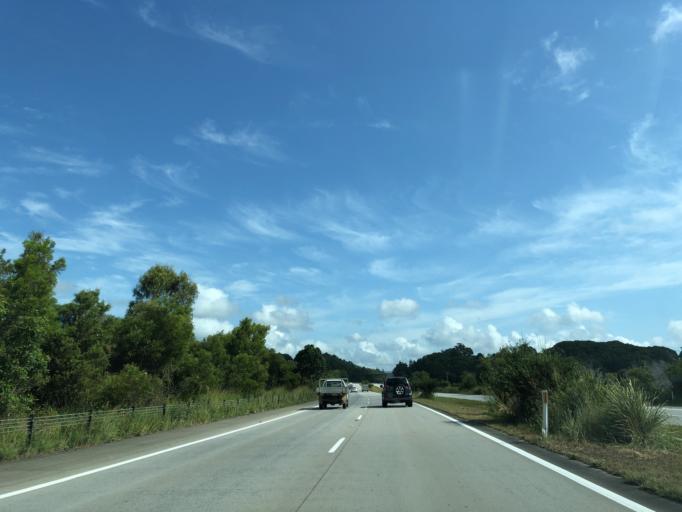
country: AU
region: New South Wales
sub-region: Byron Shire
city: Brunswick Heads
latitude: -28.5781
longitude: 153.5436
